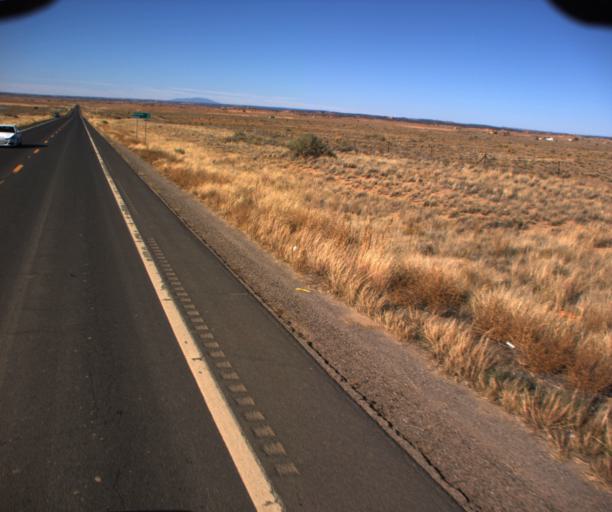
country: US
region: Arizona
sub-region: Coconino County
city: Kaibito
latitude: 36.4646
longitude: -110.6940
